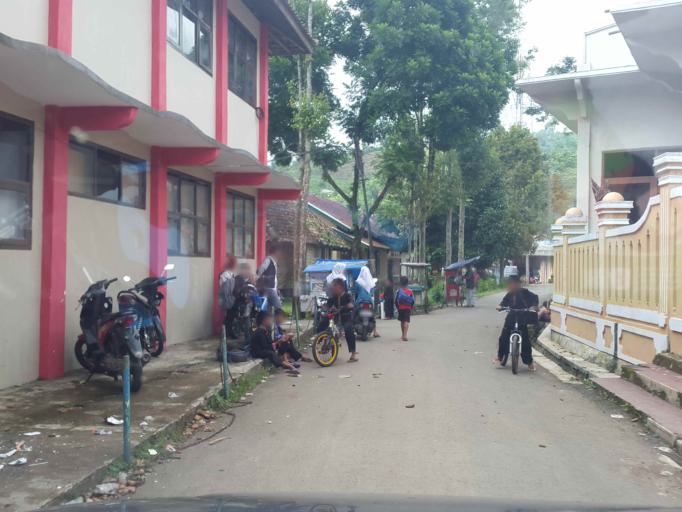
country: ID
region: West Java
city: Sukanagara
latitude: -7.1001
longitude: 107.1296
